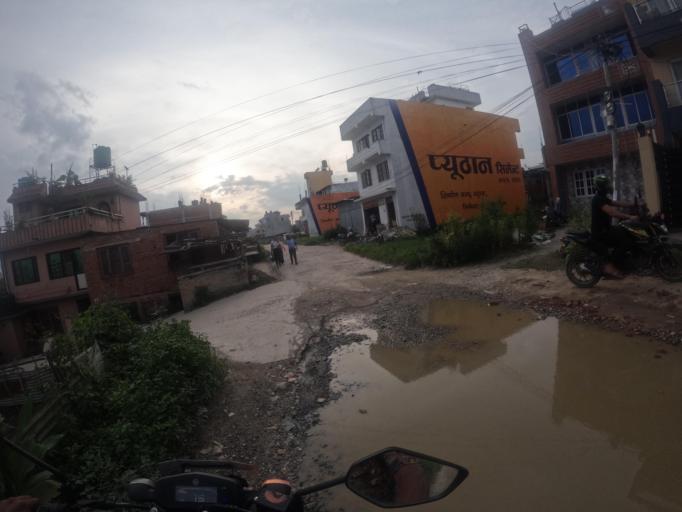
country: NP
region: Central Region
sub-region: Bagmati Zone
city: Bhaktapur
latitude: 27.6887
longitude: 85.3954
